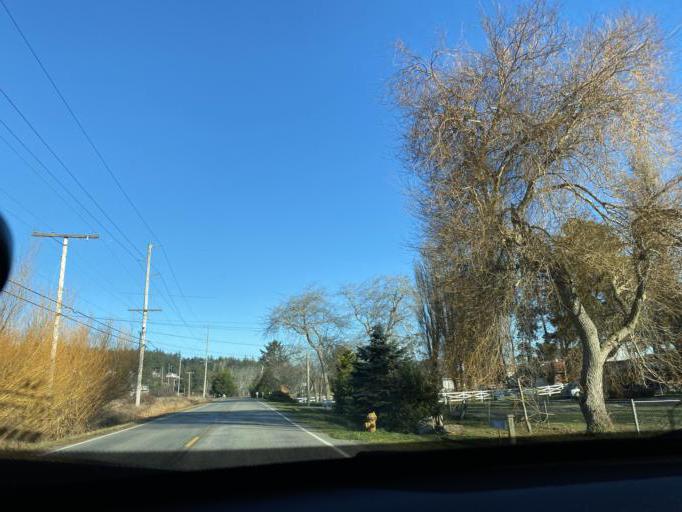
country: US
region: Washington
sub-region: Island County
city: Camano
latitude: 48.1069
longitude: -122.5714
